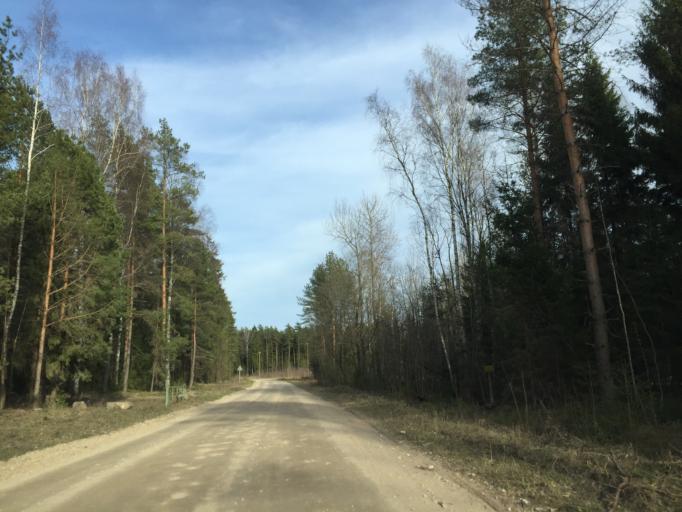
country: LV
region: Kegums
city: Kegums
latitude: 56.7947
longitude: 24.7209
